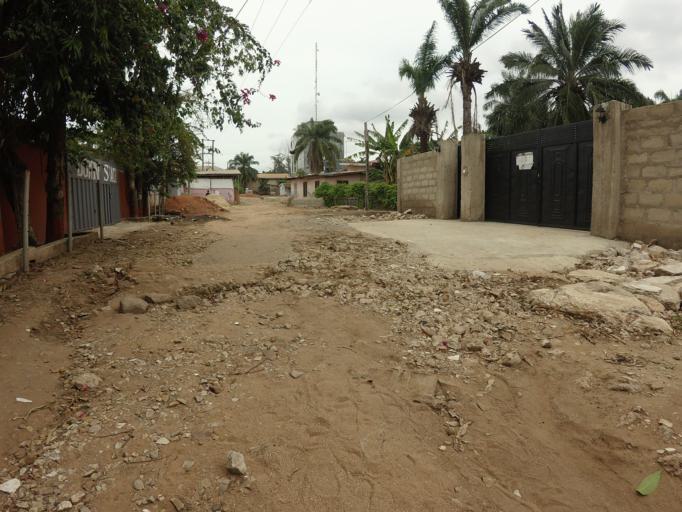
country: GH
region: Greater Accra
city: Accra
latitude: 5.6002
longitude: -0.2228
